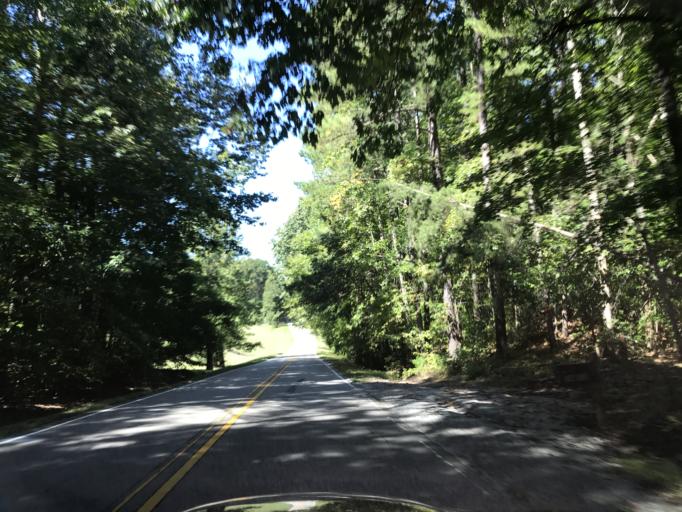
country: US
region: North Carolina
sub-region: Wake County
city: Wake Forest
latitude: 35.9492
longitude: -78.6063
